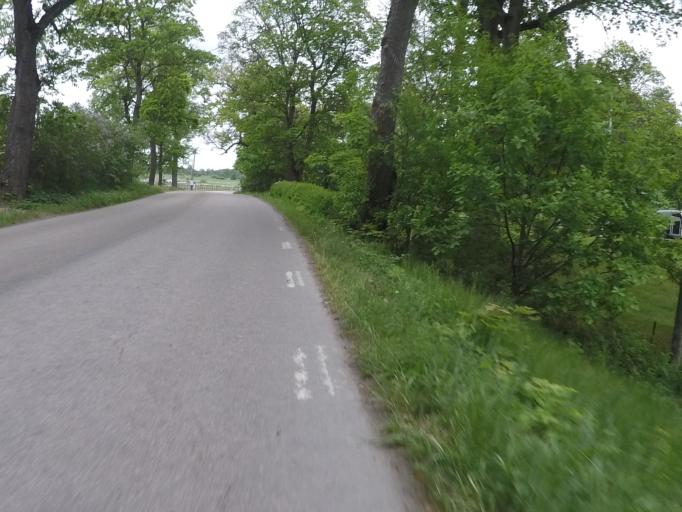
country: SE
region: Vaestmanland
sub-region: Hallstahammars Kommun
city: Kolback
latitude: 59.5286
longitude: 16.2882
